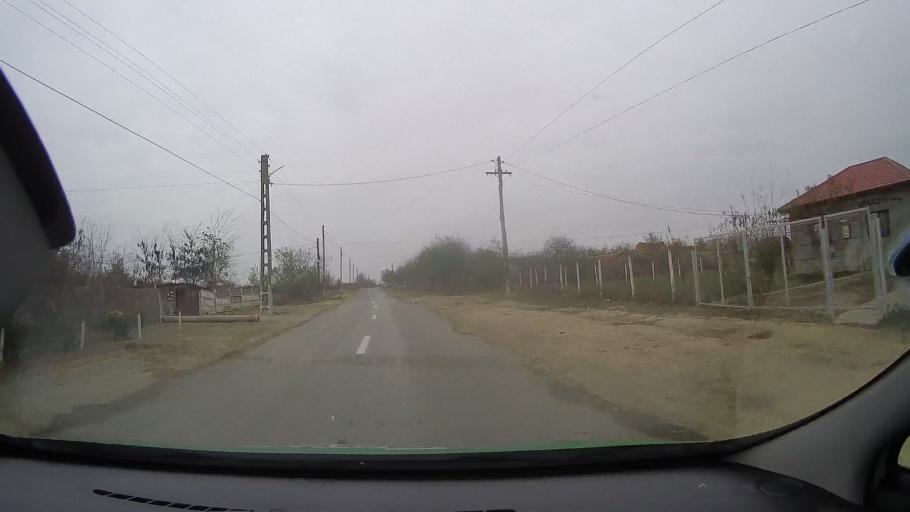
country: RO
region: Constanta
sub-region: Comuna Vulturu
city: Vulturu
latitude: 44.6532
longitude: 28.2677
